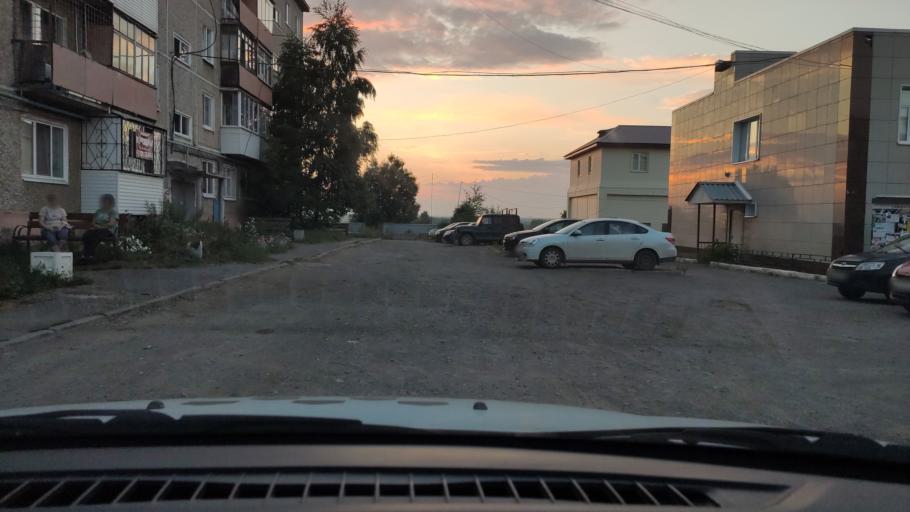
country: RU
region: Perm
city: Kondratovo
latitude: 57.9458
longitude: 56.0652
